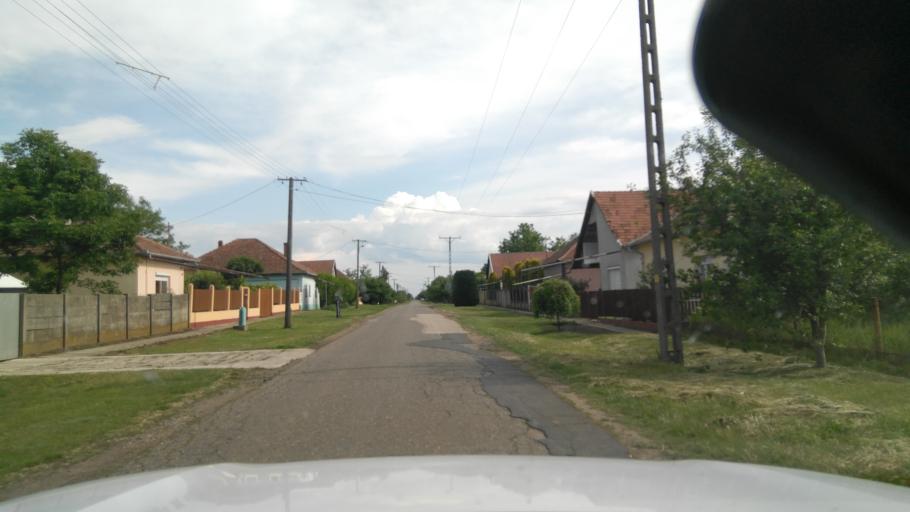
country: HU
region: Bekes
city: Ujkigyos
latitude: 46.5874
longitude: 21.0339
